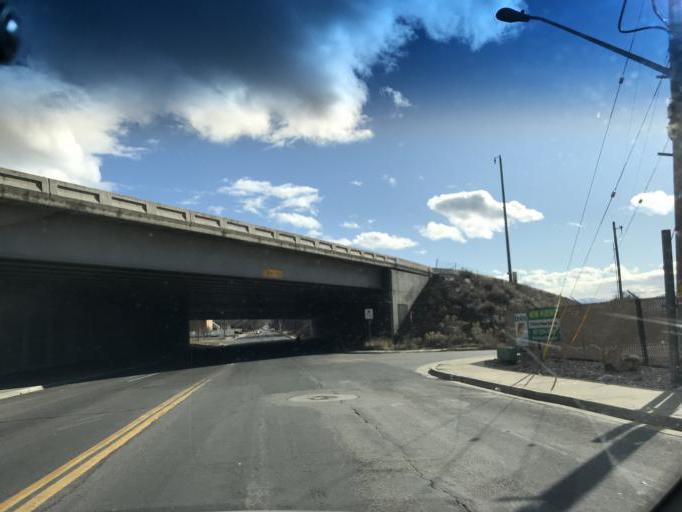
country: US
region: Utah
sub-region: Davis County
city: North Salt Lake
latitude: 40.8513
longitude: -111.9119
